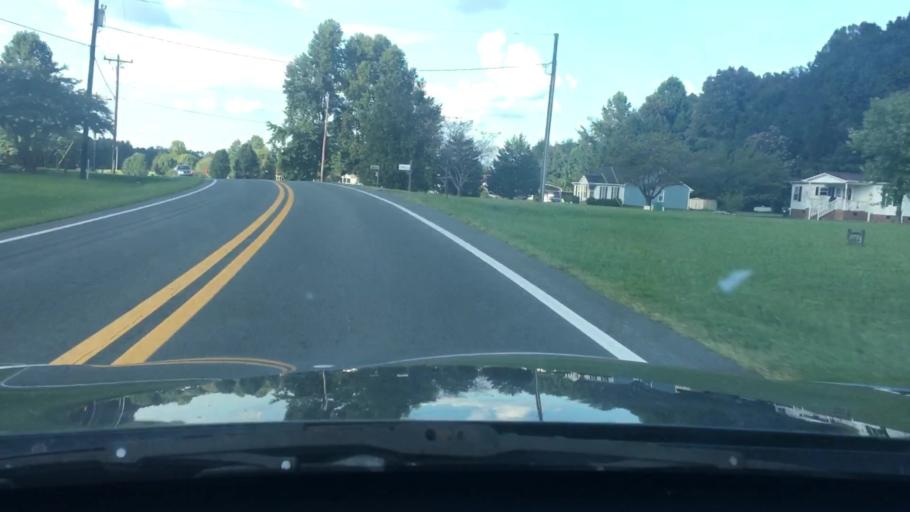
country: US
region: North Carolina
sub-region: Alamance County
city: Green Level
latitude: 36.1980
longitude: -79.3231
